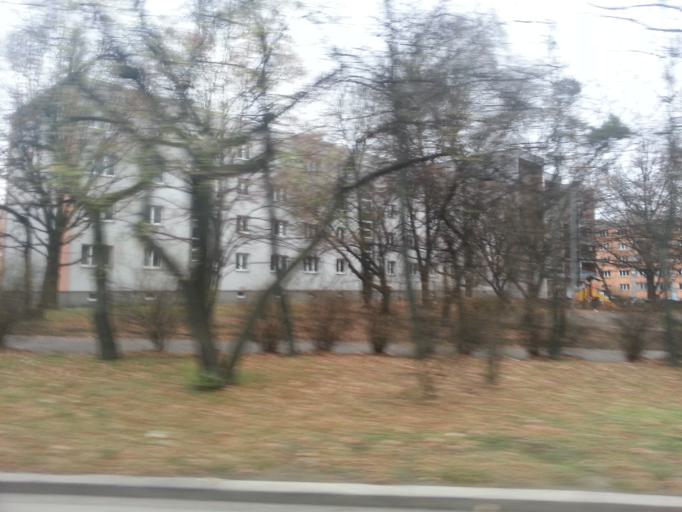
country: CZ
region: Central Bohemia
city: Horomerice
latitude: 50.0842
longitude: 14.3476
